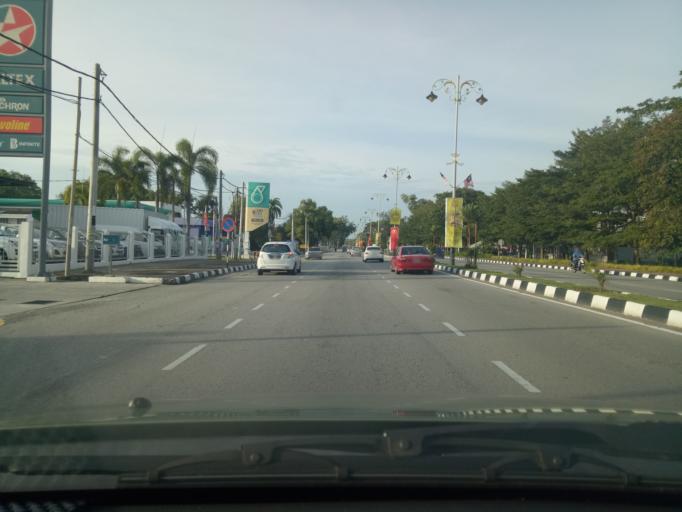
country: MY
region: Kedah
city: Alor Setar
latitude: 6.1329
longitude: 100.3686
